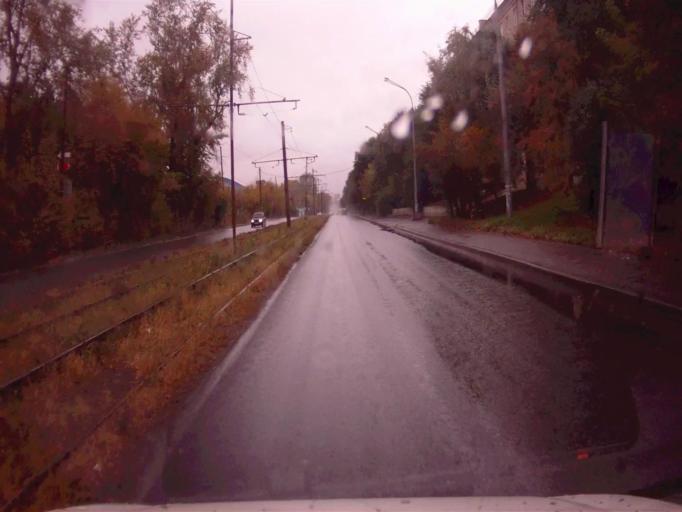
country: RU
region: Chelyabinsk
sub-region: Gorod Chelyabinsk
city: Chelyabinsk
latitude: 55.1753
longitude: 61.4151
